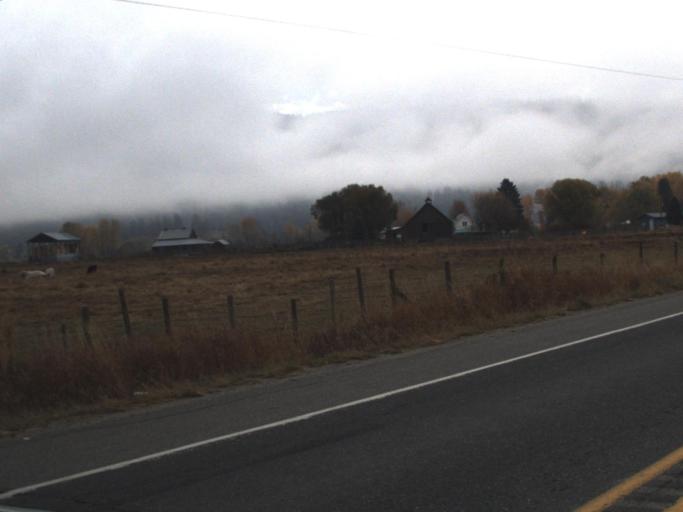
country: US
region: Washington
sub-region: Stevens County
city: Colville
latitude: 48.5801
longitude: -117.9566
